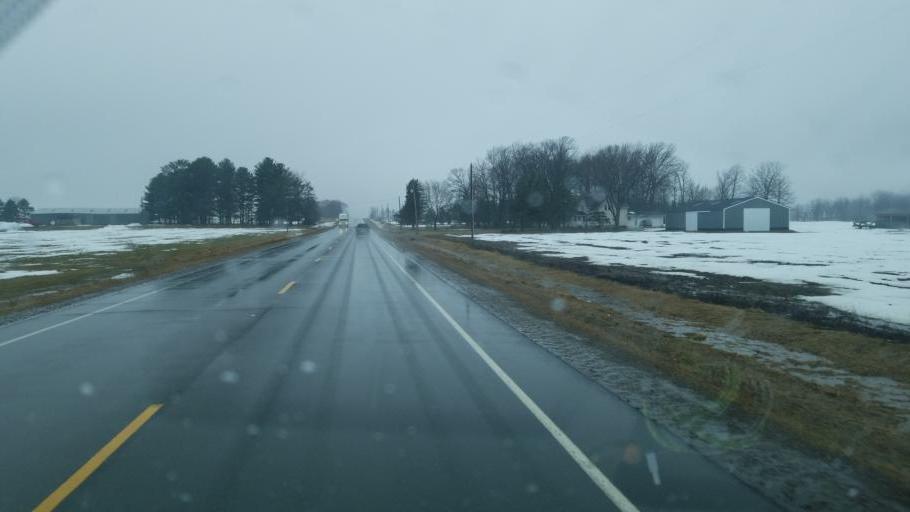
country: US
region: Wisconsin
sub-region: Marathon County
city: Spencer
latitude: 44.6561
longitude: -90.3230
